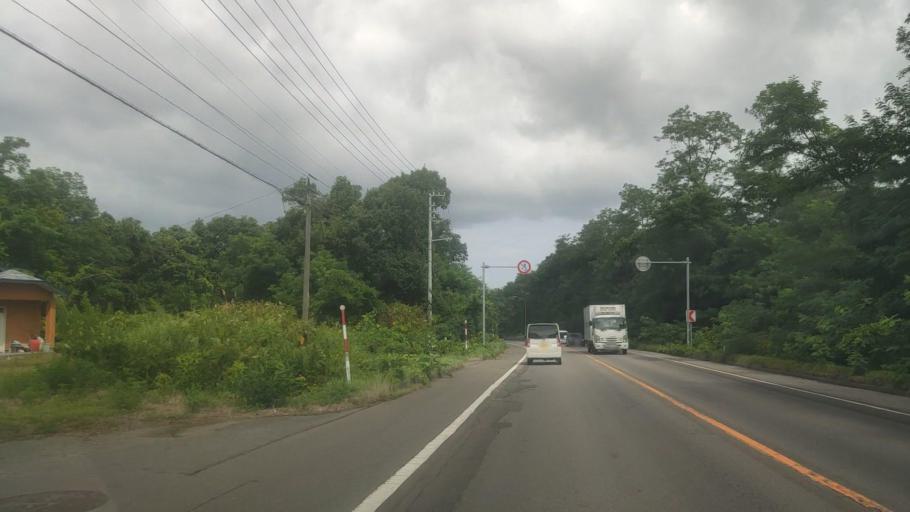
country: JP
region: Hokkaido
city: Nanae
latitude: 42.0703
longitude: 140.6030
